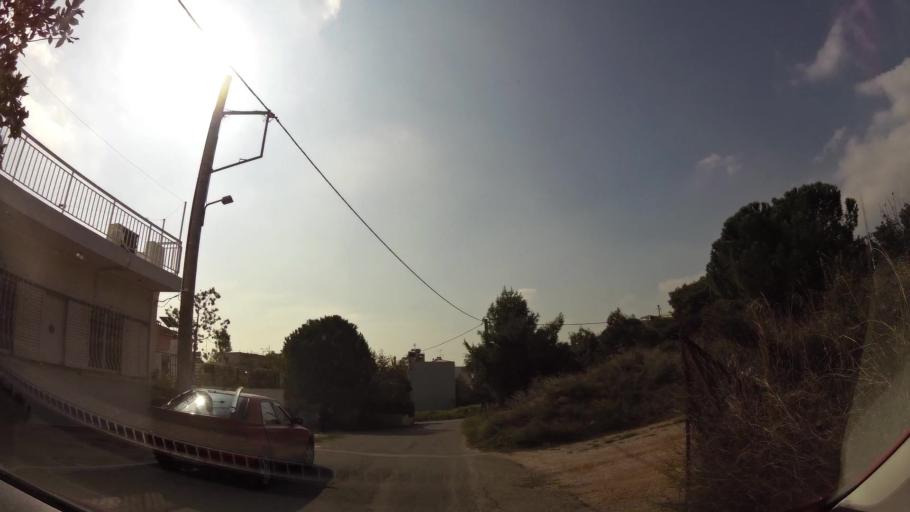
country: GR
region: Attica
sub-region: Nomarchia Dytikis Attikis
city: Zefyri
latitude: 38.0580
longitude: 23.7270
